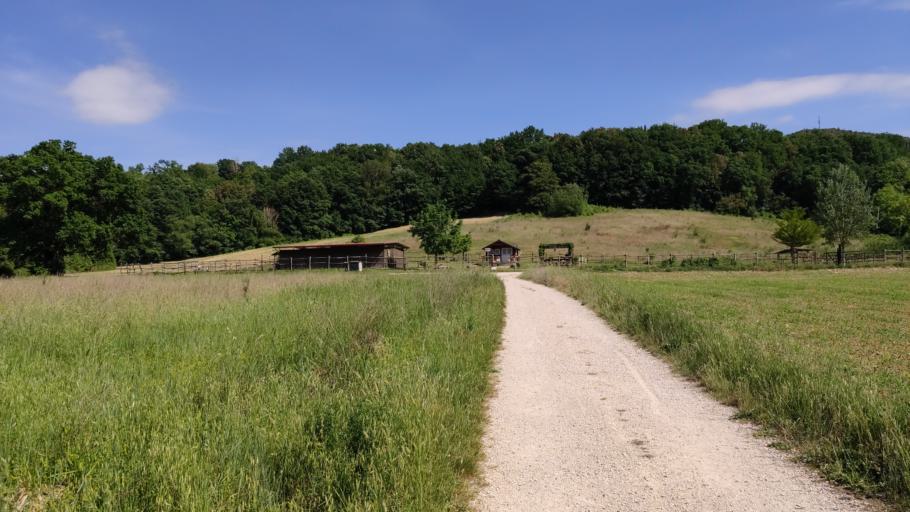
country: IT
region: Umbria
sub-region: Provincia di Terni
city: Amelia
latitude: 42.5594
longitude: 12.4199
